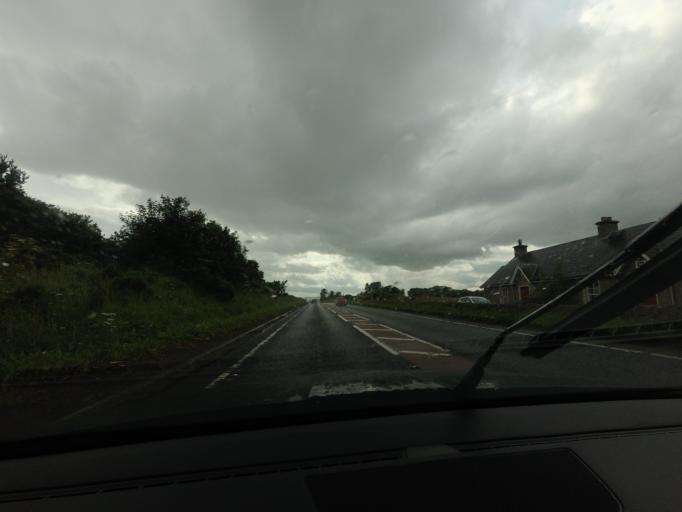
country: GB
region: Scotland
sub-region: Highland
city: Fortrose
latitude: 57.5153
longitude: -4.0873
